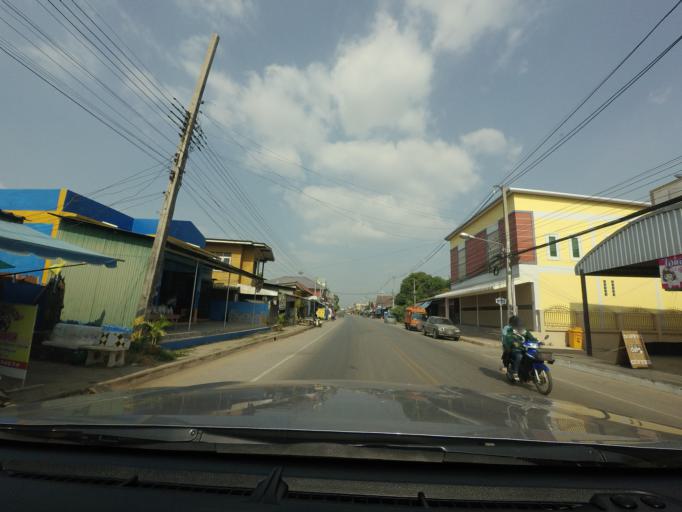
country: TH
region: Sukhothai
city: Kong Krailat
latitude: 16.9452
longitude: 99.9698
